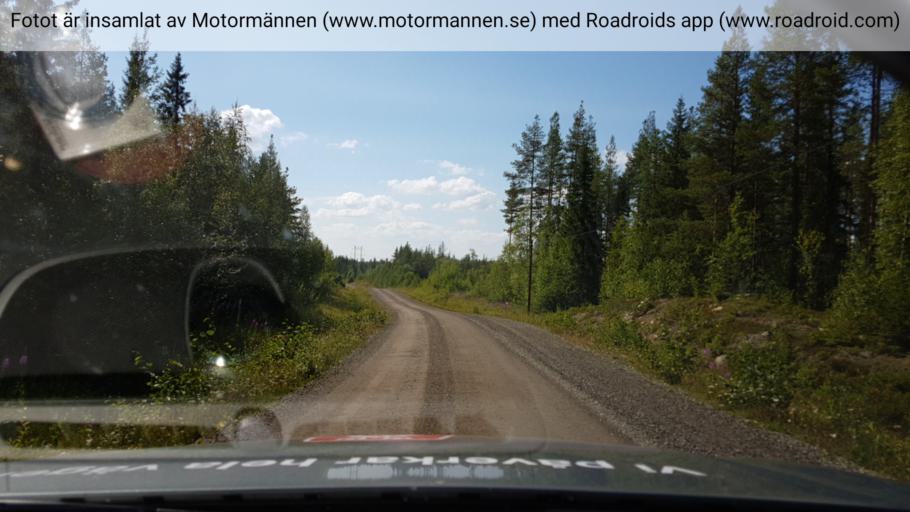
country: SE
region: Vaesterbotten
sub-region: Dorotea Kommun
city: Dorotea
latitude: 64.0955
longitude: 16.4889
